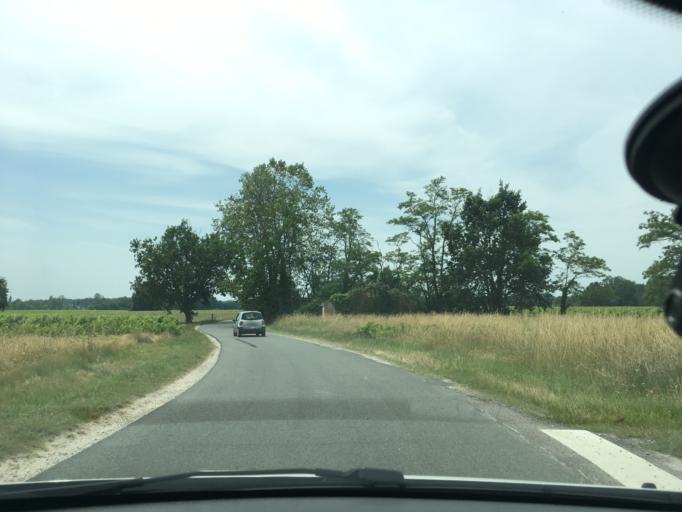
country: FR
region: Aquitaine
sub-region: Departement de la Gironde
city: Listrac-Medoc
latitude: 45.0611
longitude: -0.8028
